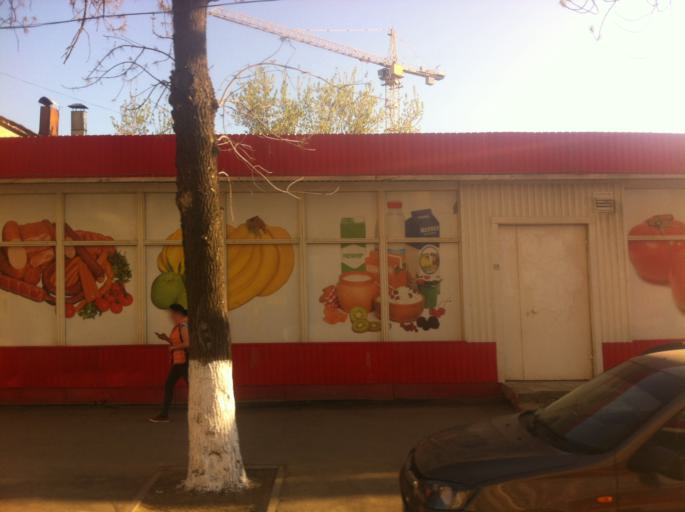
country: RU
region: Samara
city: Samara
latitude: 53.1926
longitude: 50.1035
